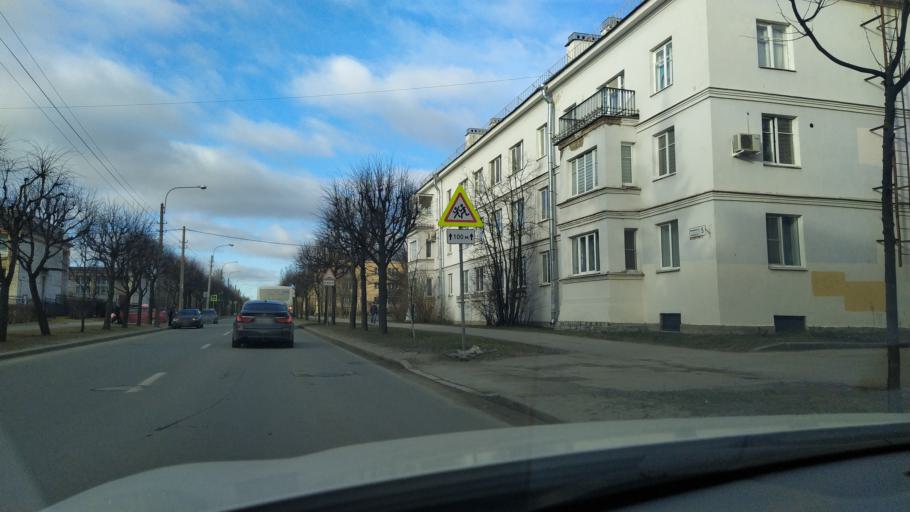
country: RU
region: St.-Petersburg
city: Pushkin
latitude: 59.7240
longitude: 30.4256
